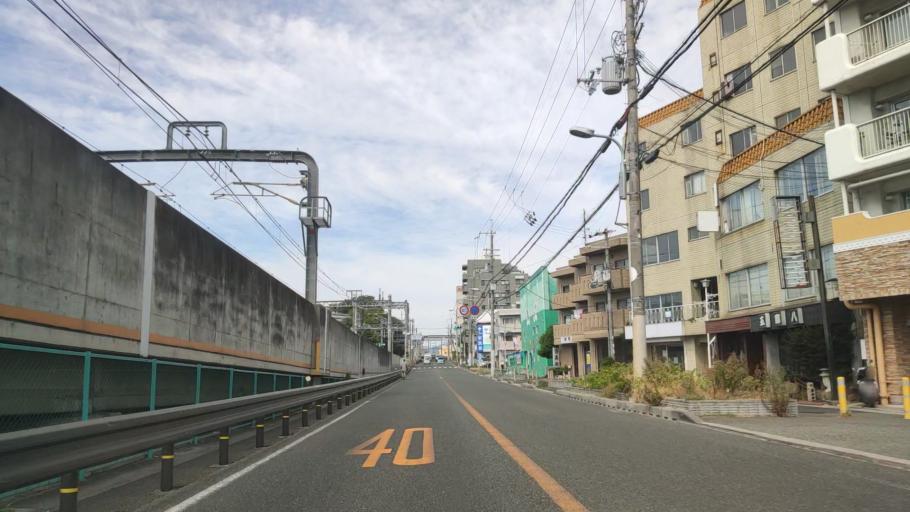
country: JP
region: Osaka
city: Toyonaka
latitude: 34.7906
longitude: 135.4542
